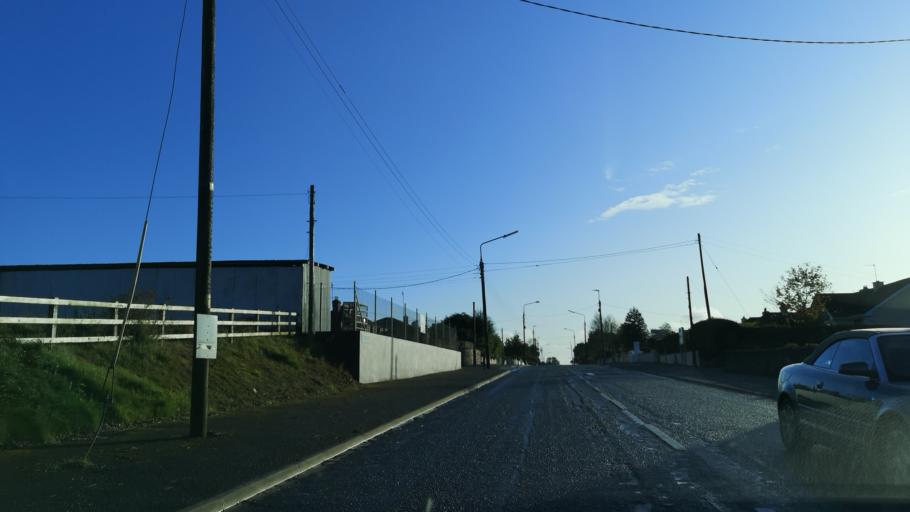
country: IE
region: Connaught
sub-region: Roscommon
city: Castlerea
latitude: 53.7766
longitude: -8.4895
